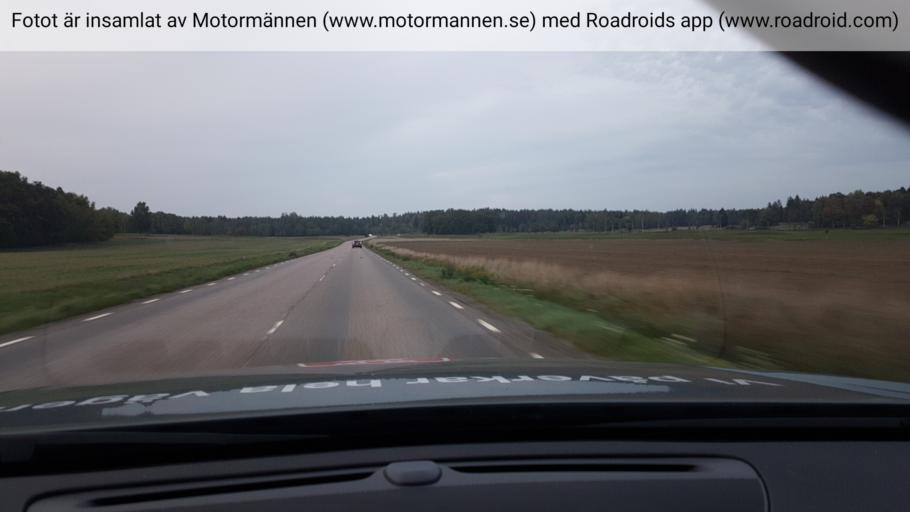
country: SE
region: Stockholm
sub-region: Haninge Kommun
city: Haninge
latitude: 59.1068
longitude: 18.1875
